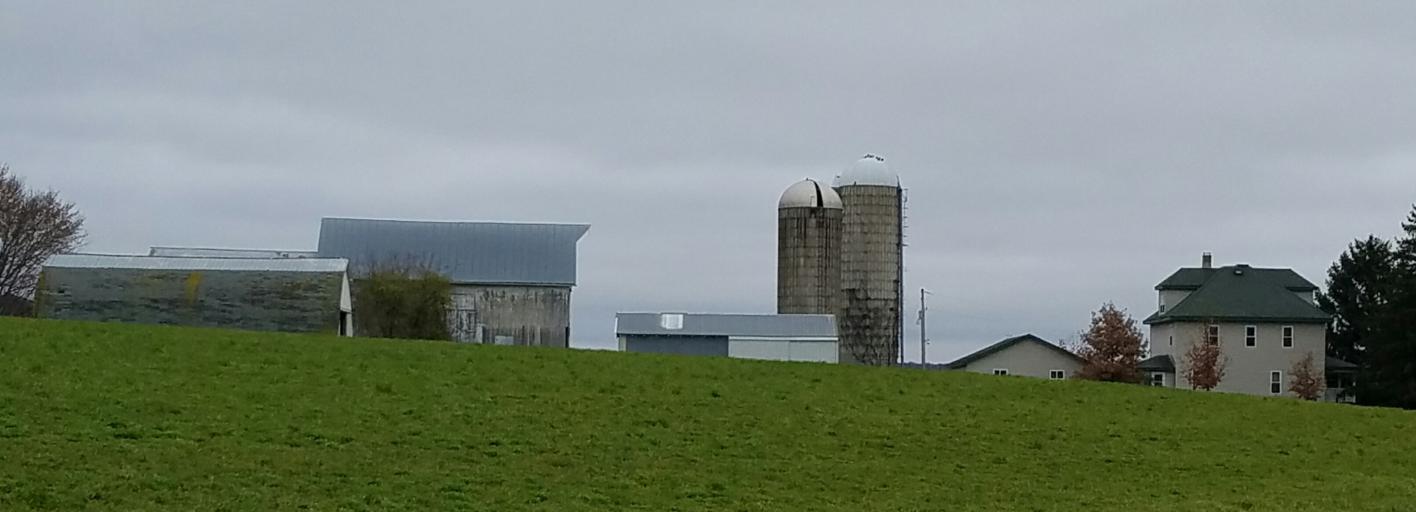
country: US
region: Wisconsin
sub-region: Vernon County
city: Hillsboro
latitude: 43.5800
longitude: -90.2605
